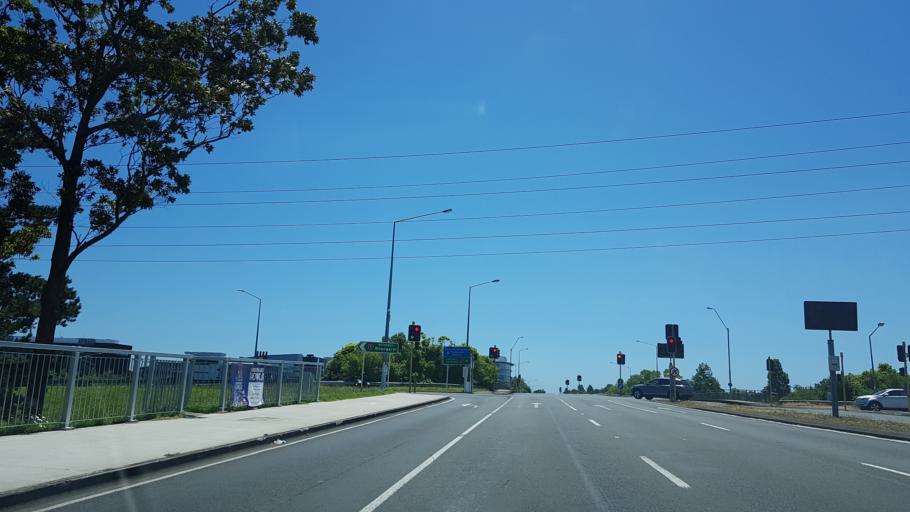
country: NZ
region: Auckland
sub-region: Auckland
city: North Shore
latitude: -36.7889
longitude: 174.7518
